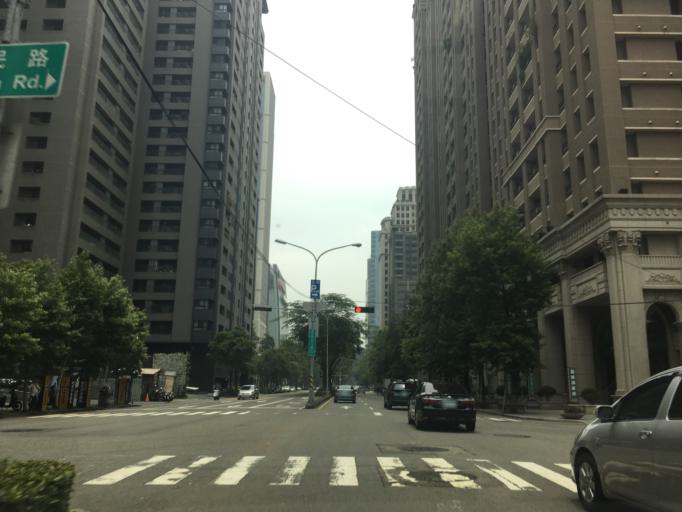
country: TW
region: Taiwan
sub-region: Taichung City
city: Taichung
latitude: 24.1652
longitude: 120.6406
